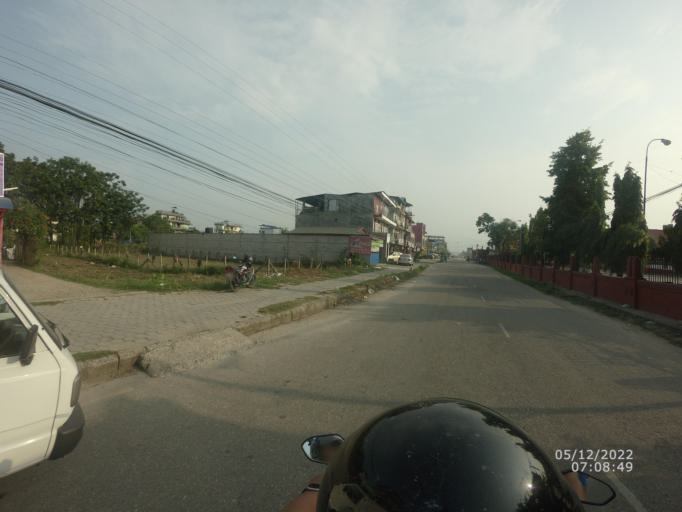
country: NP
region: Central Region
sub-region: Narayani Zone
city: Bharatpur
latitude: 27.6677
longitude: 84.4382
